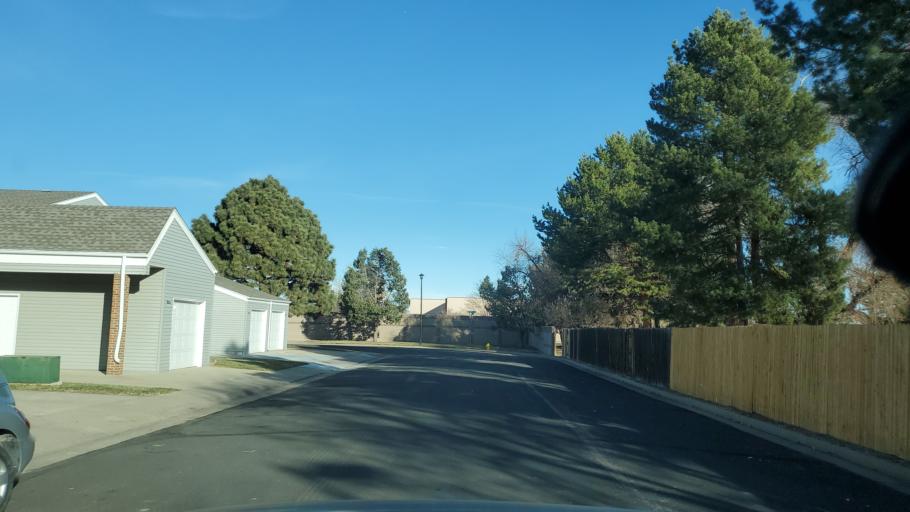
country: US
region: Colorado
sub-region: Adams County
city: Northglenn
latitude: 39.9129
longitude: -104.9438
